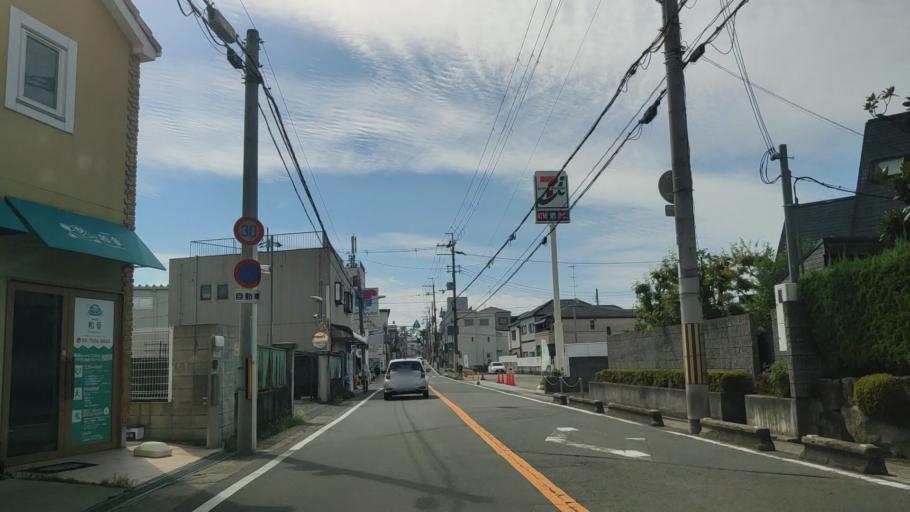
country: JP
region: Osaka
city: Toyonaka
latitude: 34.7951
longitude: 135.4645
